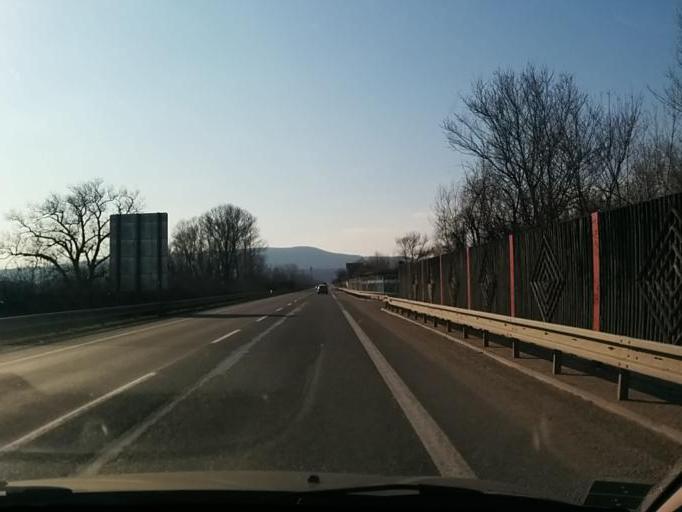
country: SK
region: Trenciansky
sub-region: Okres Nove Mesto nad Vahom
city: Nove Mesto nad Vahom
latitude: 48.7628
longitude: 17.8612
